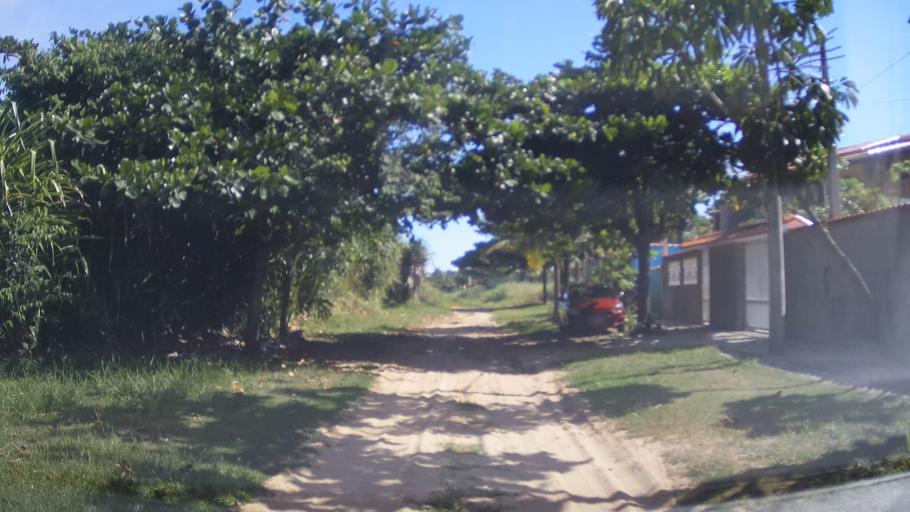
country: BR
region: Sao Paulo
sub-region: Itanhaem
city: Itanhaem
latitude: -24.1617
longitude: -46.7430
